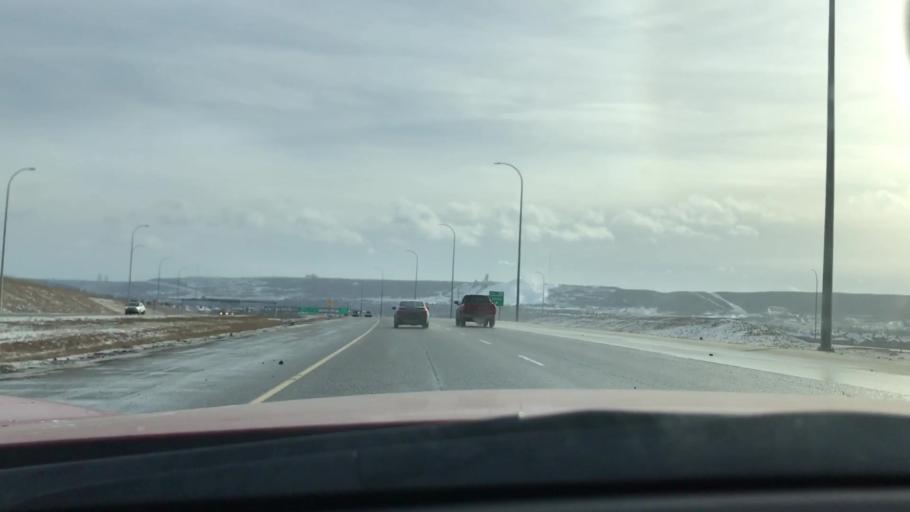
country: CA
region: Alberta
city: Calgary
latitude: 51.1173
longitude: -114.2303
